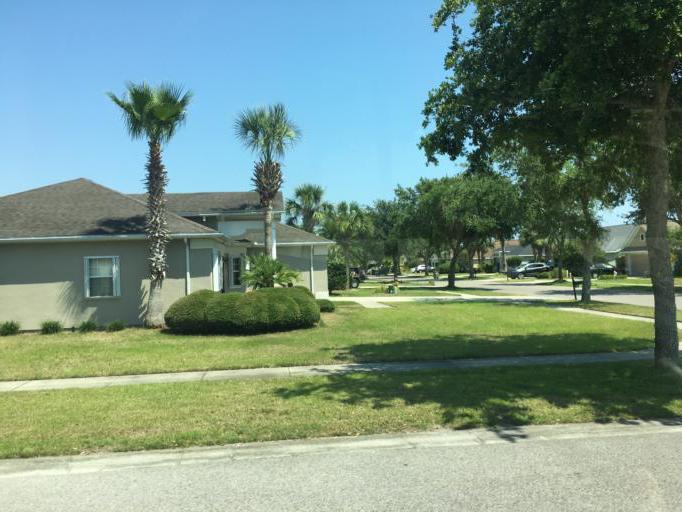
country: US
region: Florida
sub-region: Bay County
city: Laguna Beach
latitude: 30.2188
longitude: -85.8604
